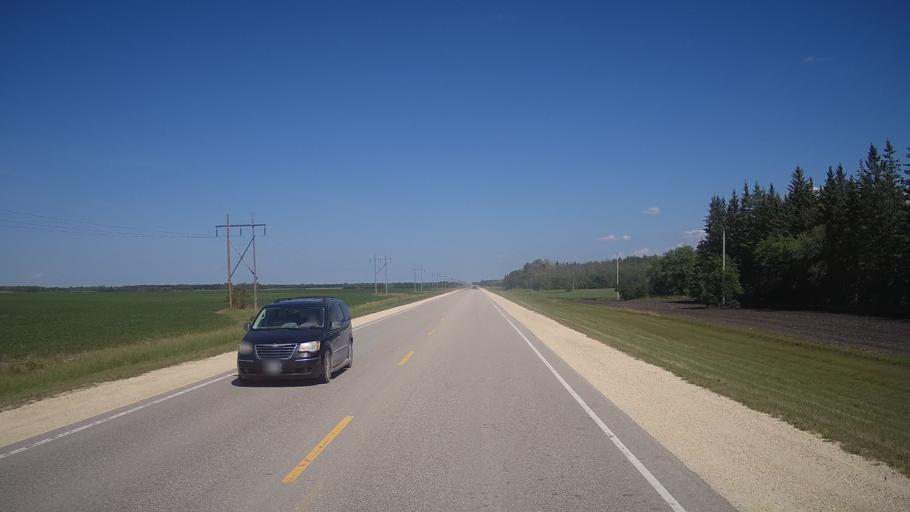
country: CA
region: Manitoba
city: Stonewall
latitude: 50.1227
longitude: -97.3899
